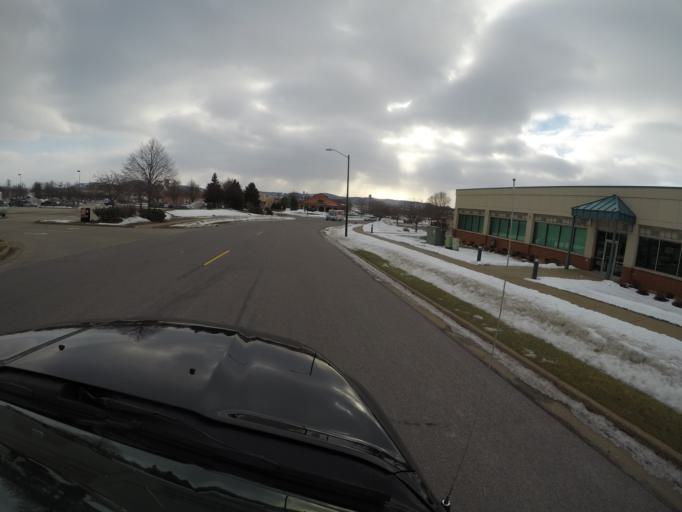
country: US
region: Wisconsin
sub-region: La Crosse County
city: Onalaska
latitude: 43.8798
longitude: -91.1877
